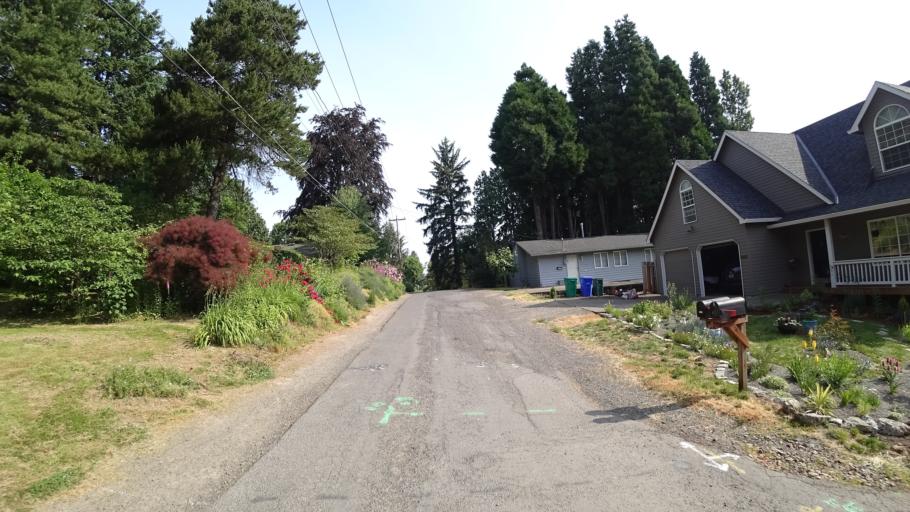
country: US
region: Oregon
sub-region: Washington County
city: Garden Home-Whitford
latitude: 45.4626
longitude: -122.7128
